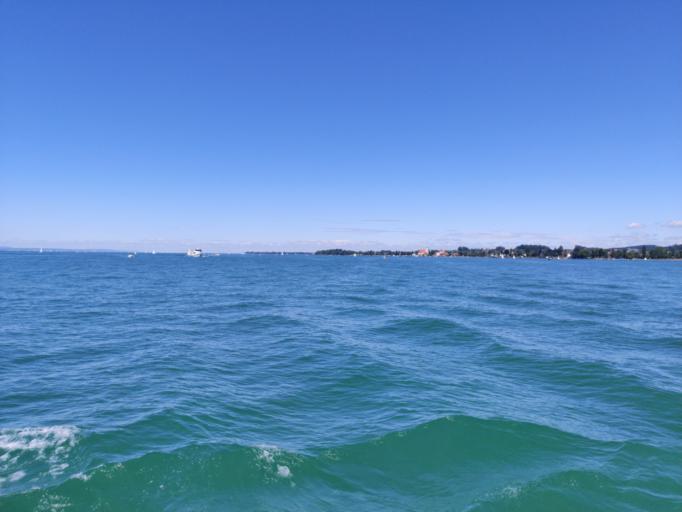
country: DE
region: Bavaria
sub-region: Swabia
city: Bodolz
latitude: 47.5543
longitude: 9.6461
